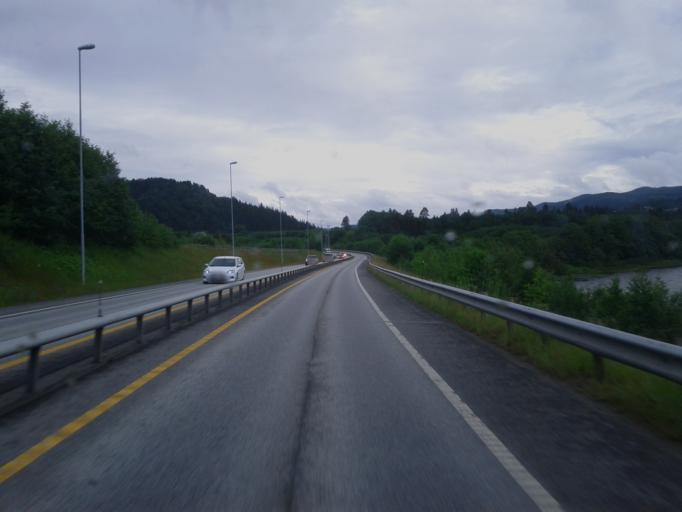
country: NO
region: Sor-Trondelag
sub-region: Melhus
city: Melhus
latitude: 63.2611
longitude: 10.2856
